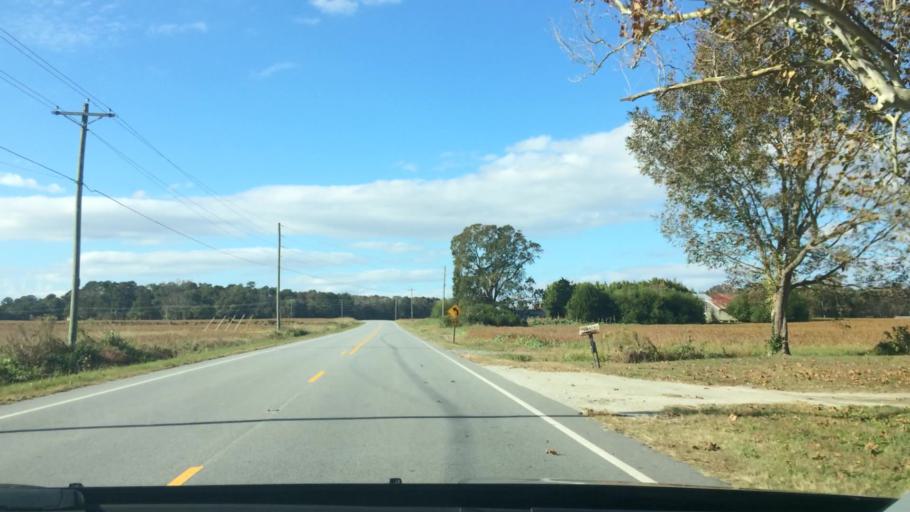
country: US
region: North Carolina
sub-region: Greene County
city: Maury
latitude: 35.4816
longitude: -77.5633
